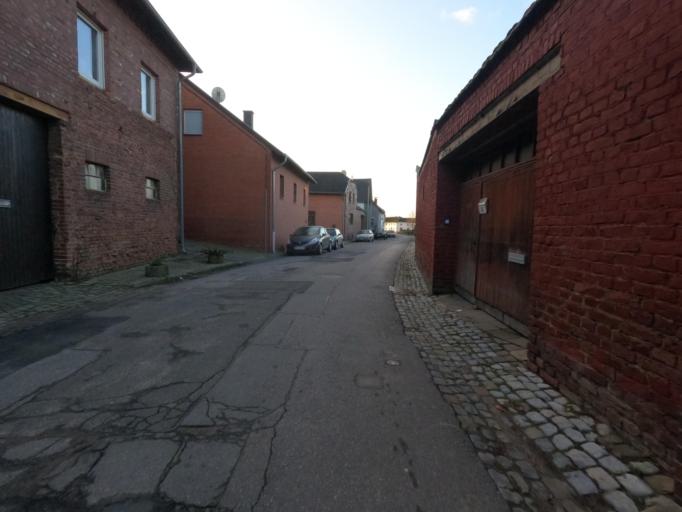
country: DE
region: North Rhine-Westphalia
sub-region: Regierungsbezirk Koln
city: Titz
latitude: 50.9896
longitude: 6.3903
